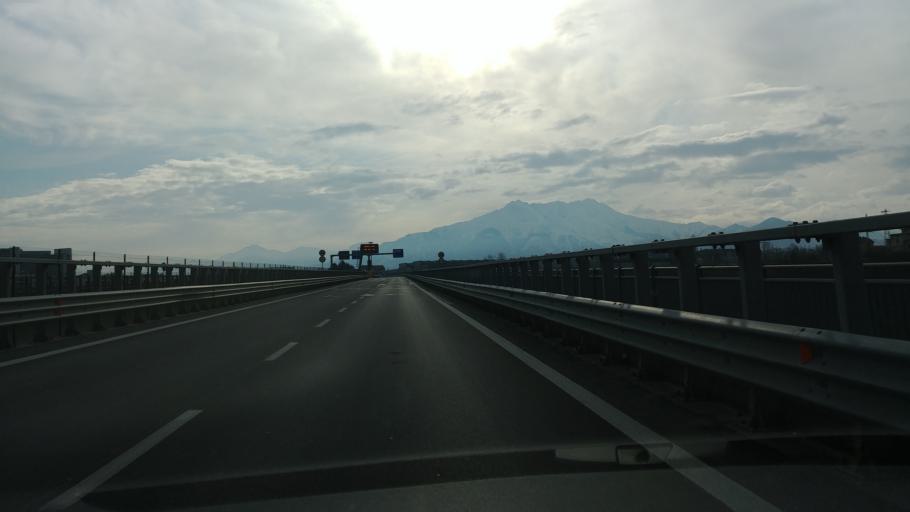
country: IT
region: Piedmont
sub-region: Provincia di Cuneo
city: Cuneo
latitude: 44.3840
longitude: 7.5242
